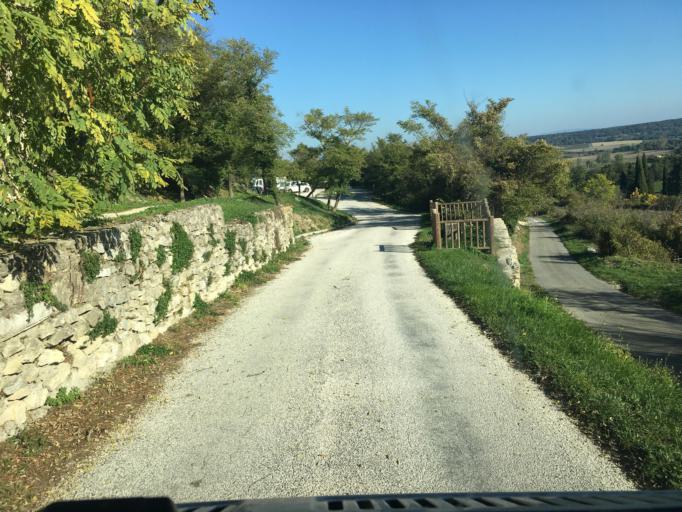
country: FR
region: Languedoc-Roussillon
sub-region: Departement du Gard
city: Goudargues
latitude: 44.1534
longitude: 4.3675
